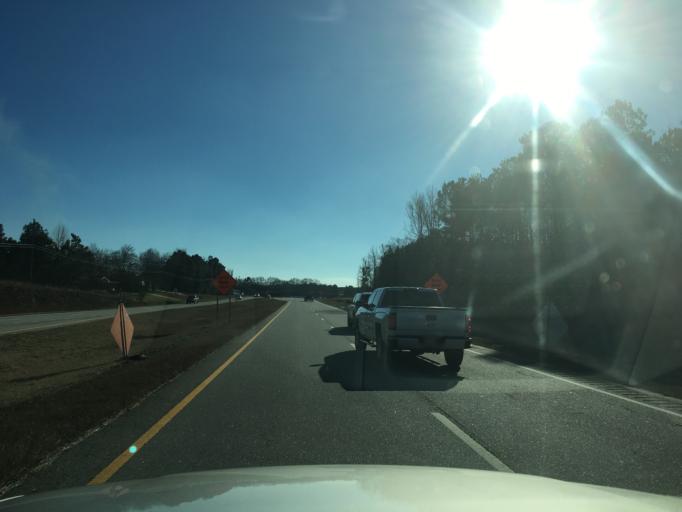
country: US
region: Georgia
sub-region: Carroll County
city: Carrollton
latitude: 33.5041
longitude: -85.0803
